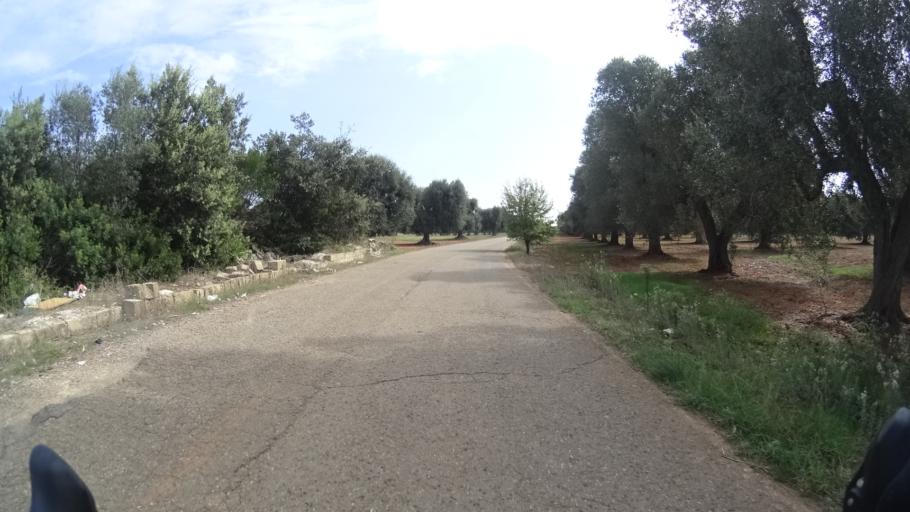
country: IT
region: Apulia
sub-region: Provincia di Taranto
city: San Marzano di San Giuseppe
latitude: 40.4381
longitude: 17.5318
